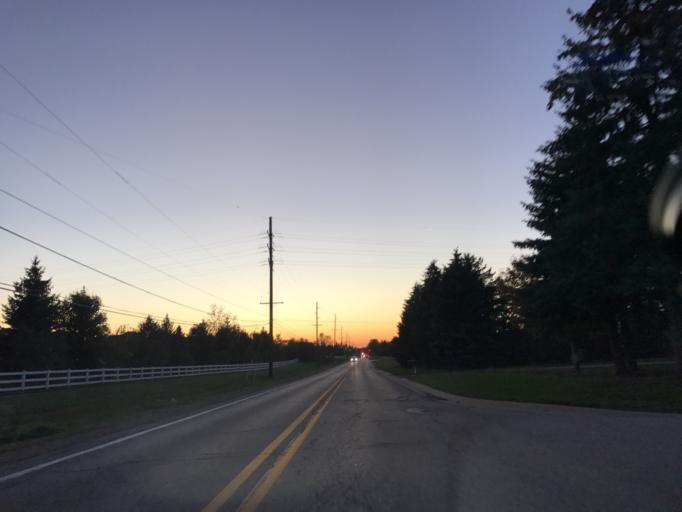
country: US
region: Michigan
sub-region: Oakland County
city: South Lyon
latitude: 42.4758
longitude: -83.6313
